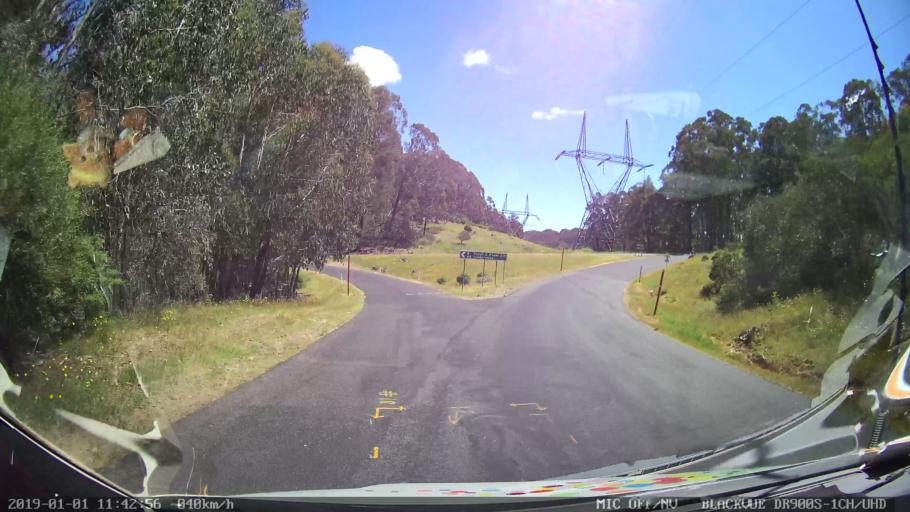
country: AU
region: New South Wales
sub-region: Snowy River
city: Jindabyne
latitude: -35.9062
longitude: 148.3836
